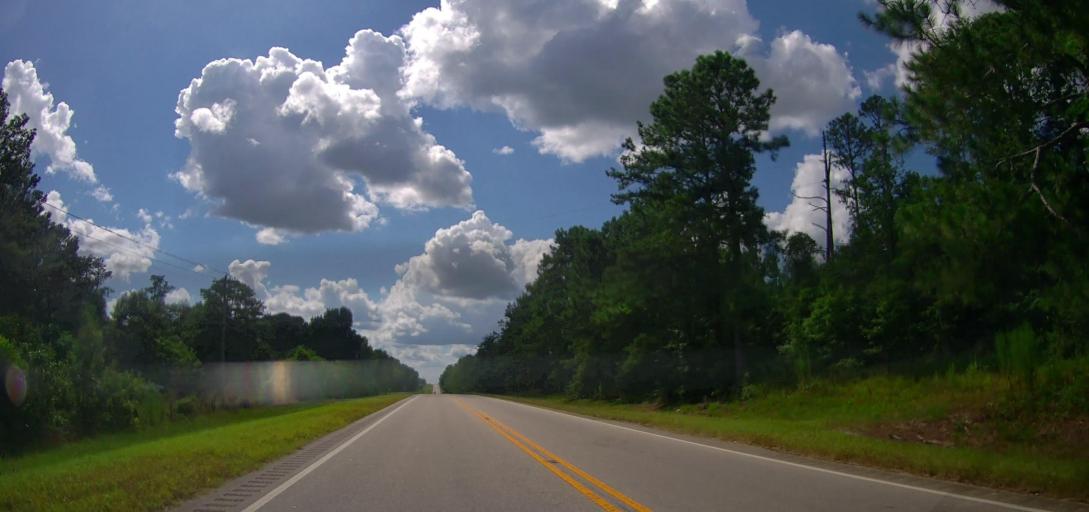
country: US
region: Alabama
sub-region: Macon County
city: Tuskegee
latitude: 32.4593
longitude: -85.5510
